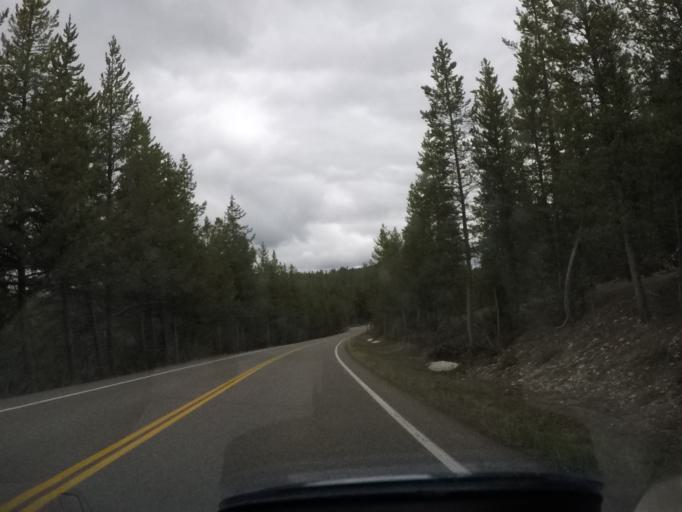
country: US
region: Wyoming
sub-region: Teton County
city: Moose Wilson Road
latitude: 43.9470
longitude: -110.6348
